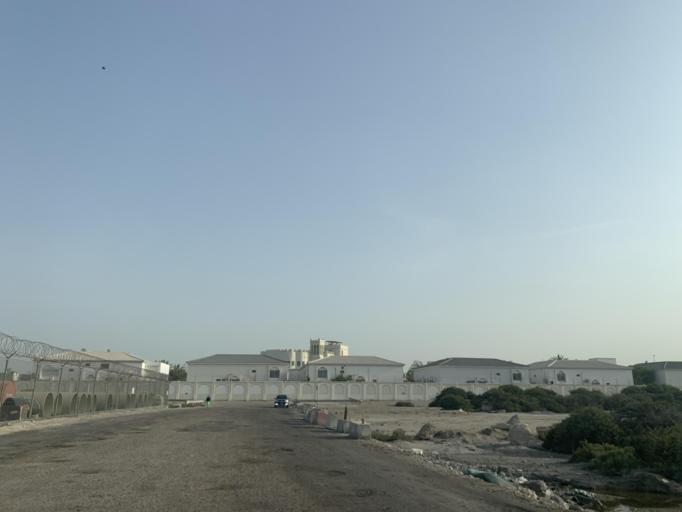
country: BH
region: Manama
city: Jidd Hafs
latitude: 26.1962
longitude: 50.5595
